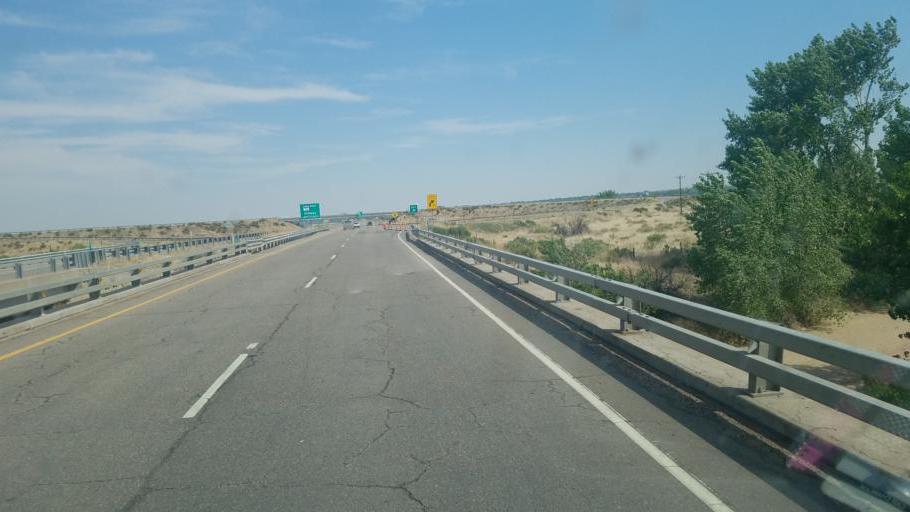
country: US
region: Colorado
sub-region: Pueblo County
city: Pueblo
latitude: 38.2654
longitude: -104.3727
